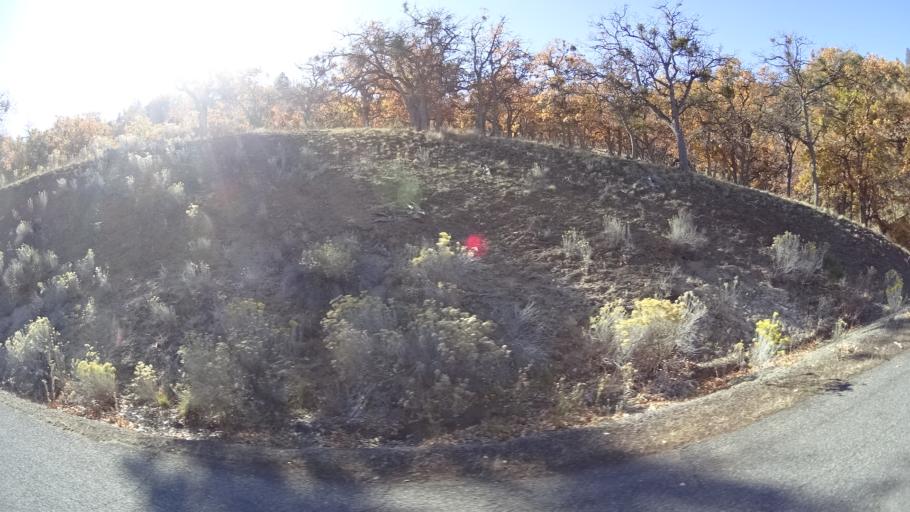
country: US
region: California
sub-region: Siskiyou County
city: Montague
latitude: 41.9791
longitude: -122.3076
